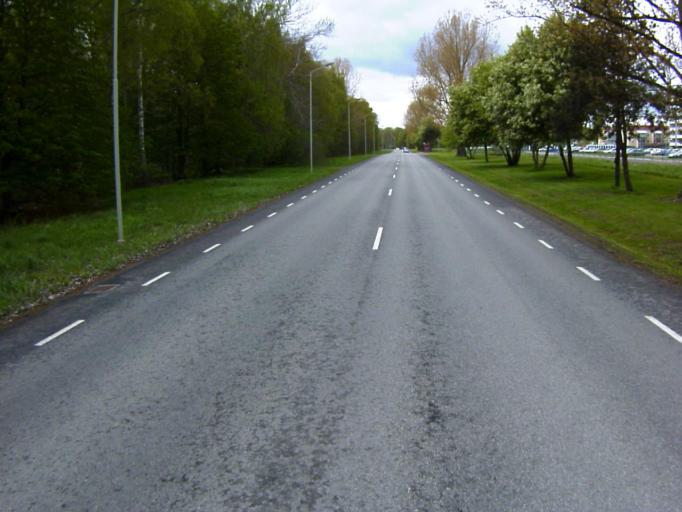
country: SE
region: Skane
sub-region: Kristianstads Kommun
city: Kristianstad
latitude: 56.0397
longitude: 14.1823
